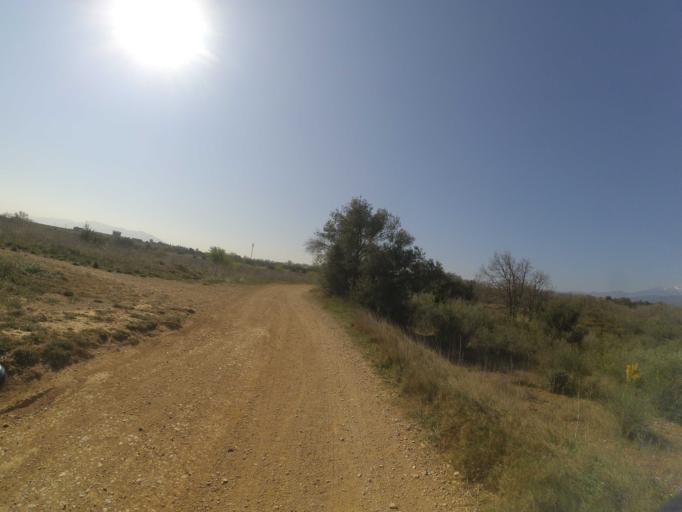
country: FR
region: Languedoc-Roussillon
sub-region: Departement des Pyrenees-Orientales
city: Llupia
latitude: 42.6143
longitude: 2.7641
